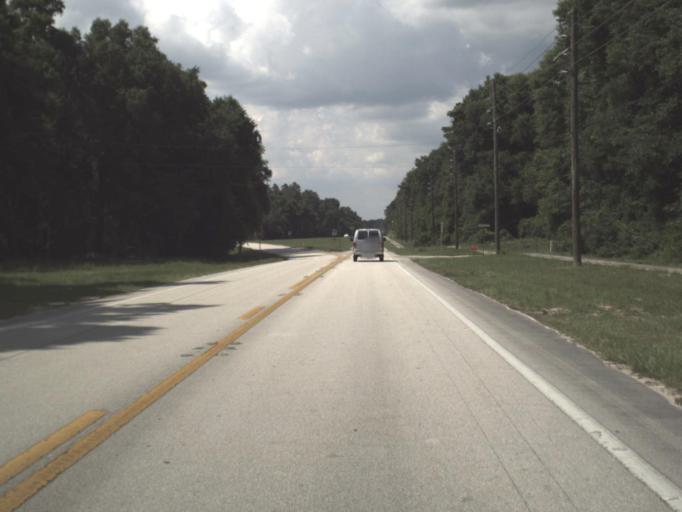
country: US
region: Florida
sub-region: Bradford County
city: Starke
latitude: 29.9609
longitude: -82.0163
